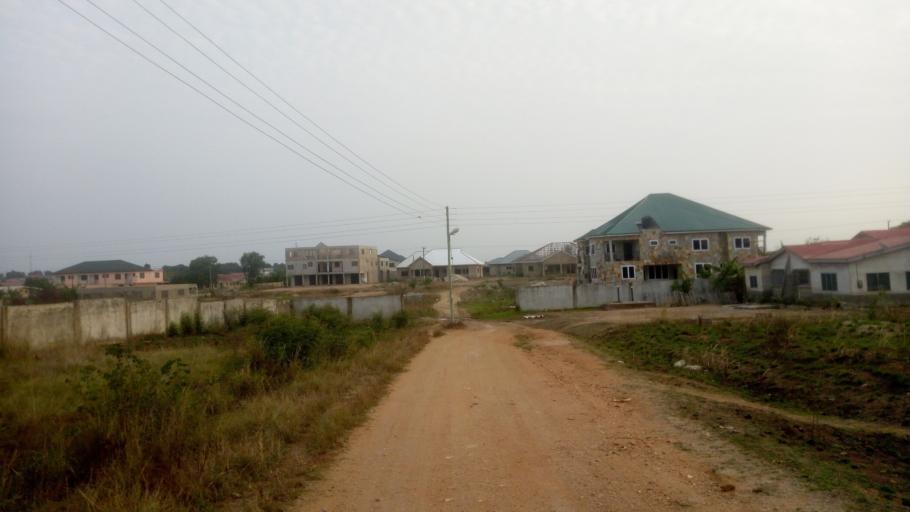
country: GH
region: Central
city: Winneba
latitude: 5.3819
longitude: -0.6287
